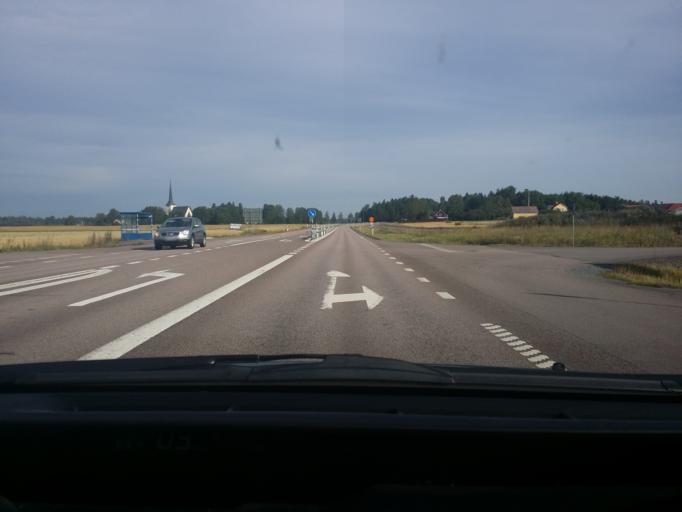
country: SE
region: Vaestmanland
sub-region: Vasteras
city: Hokasen
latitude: 59.7256
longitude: 16.5697
